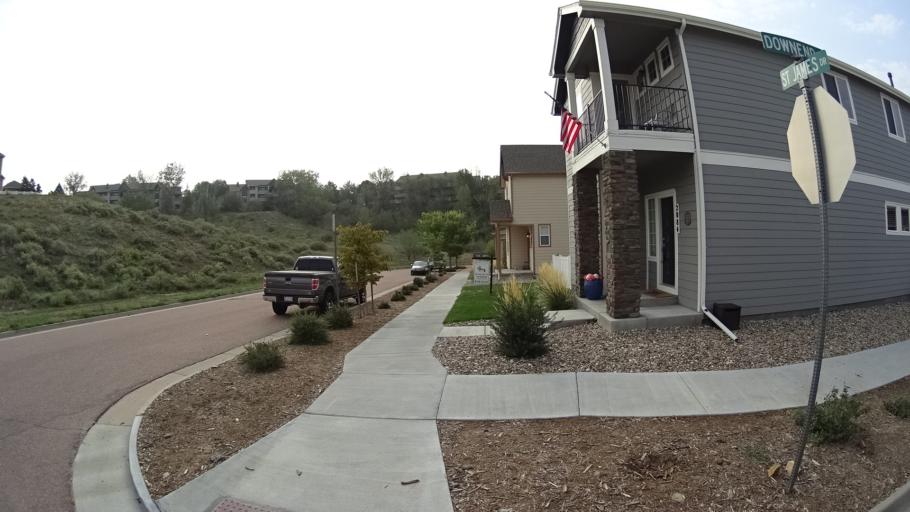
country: US
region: Colorado
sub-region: El Paso County
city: Stratmoor
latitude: 38.8054
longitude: -104.7838
